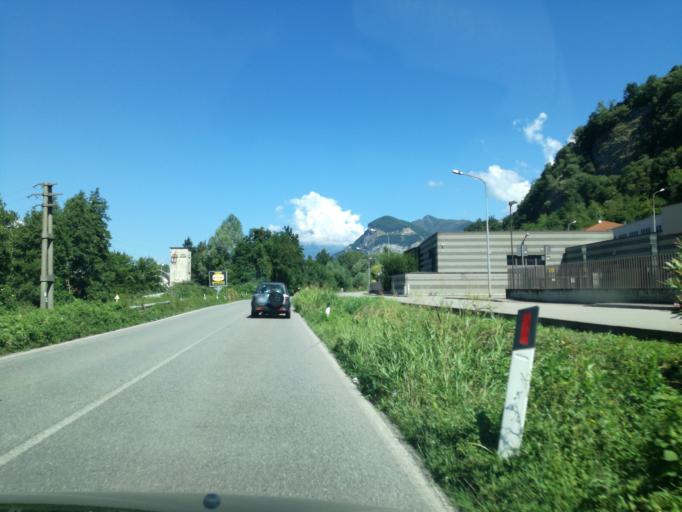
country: IT
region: Lombardy
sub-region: Provincia di Lecco
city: Monte Marenzo
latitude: 45.7709
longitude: 9.4437
